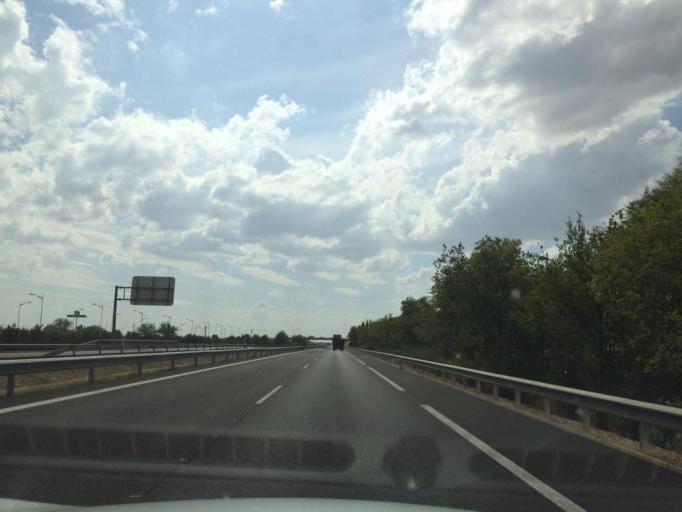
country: ES
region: Castille-La Mancha
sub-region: Provincia de Albacete
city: Albacete
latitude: 39.0093
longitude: -1.8824
